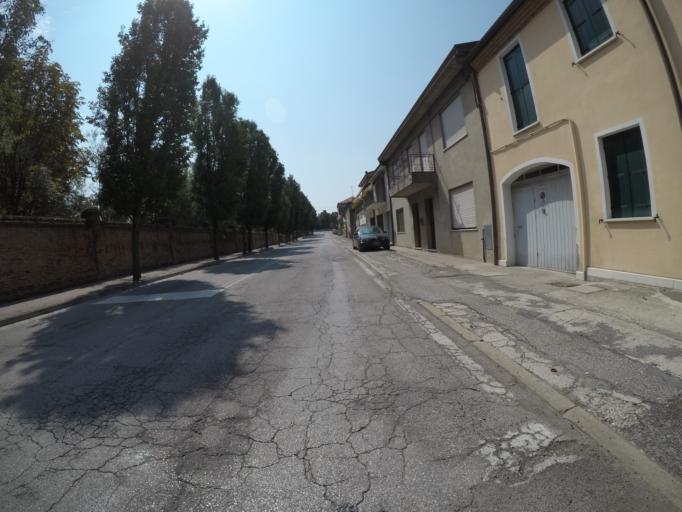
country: IT
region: Veneto
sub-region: Provincia di Rovigo
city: Lendinara
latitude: 45.0856
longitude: 11.5944
